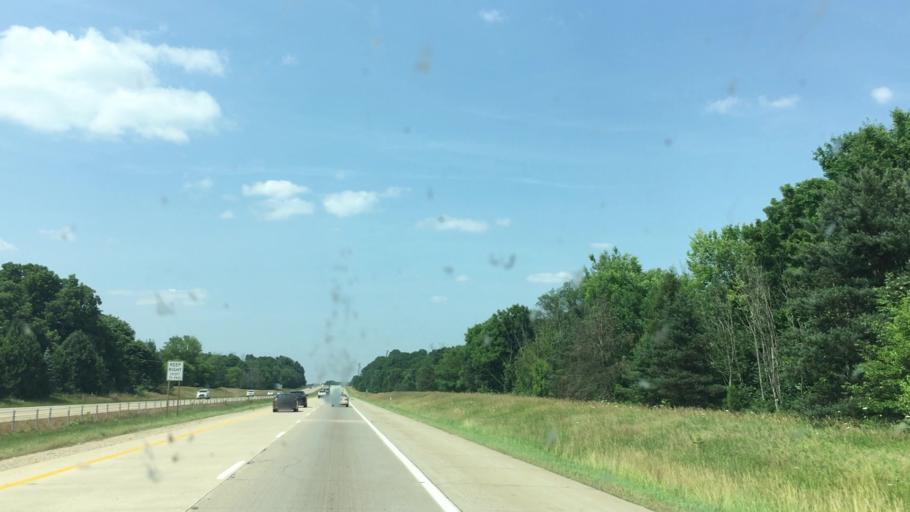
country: US
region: Michigan
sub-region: Allegan County
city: Plainwell
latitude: 42.4773
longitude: -85.6526
